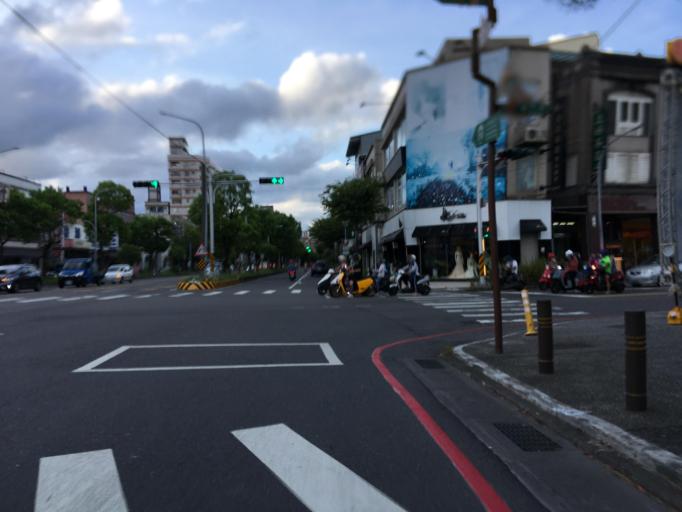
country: TW
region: Taiwan
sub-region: Yilan
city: Yilan
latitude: 24.6726
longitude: 121.7640
